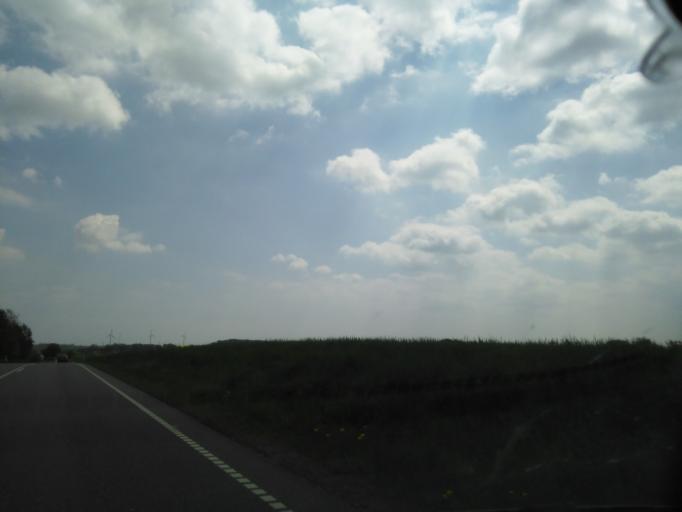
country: DK
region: Central Jutland
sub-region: Skanderborg Kommune
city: Stilling
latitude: 55.9982
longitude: 10.0108
